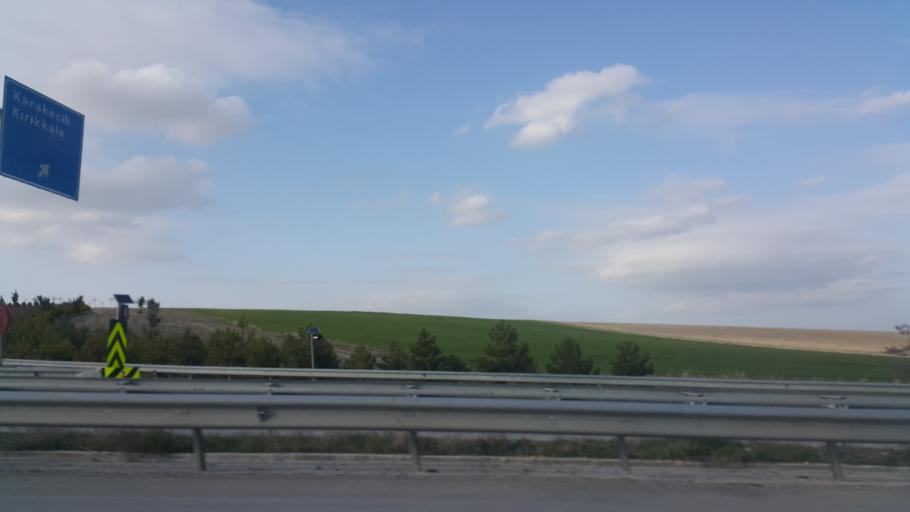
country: TR
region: Konya
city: Kulu
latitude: 39.1779
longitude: 33.1381
